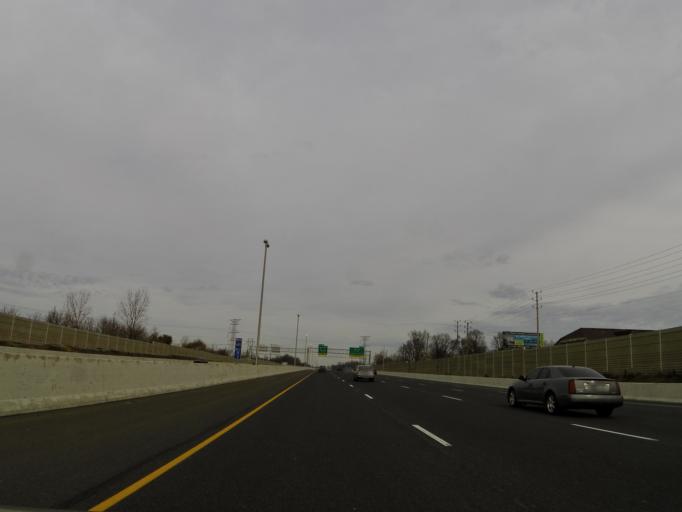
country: US
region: Indiana
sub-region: Marion County
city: Speedway
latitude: 39.8400
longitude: -86.2759
